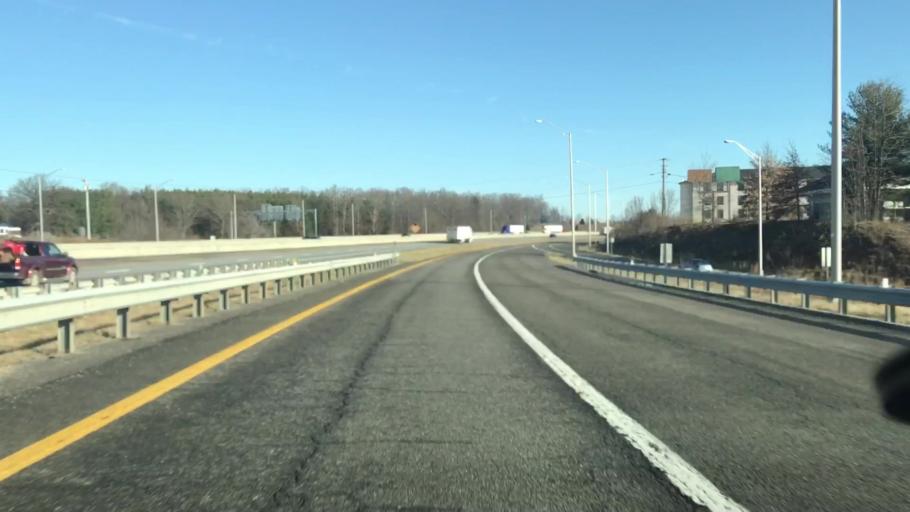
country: US
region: Virginia
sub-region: Montgomery County
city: Christiansburg
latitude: 37.1394
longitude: -80.3547
